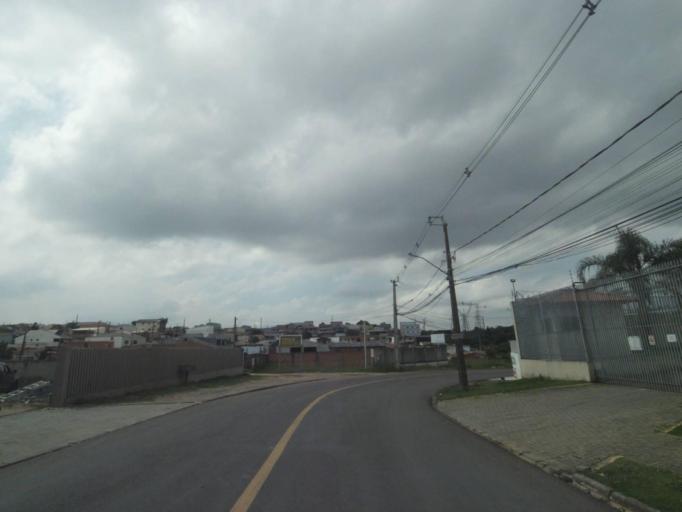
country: BR
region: Parana
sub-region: Curitiba
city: Curitiba
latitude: -25.5039
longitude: -49.3433
